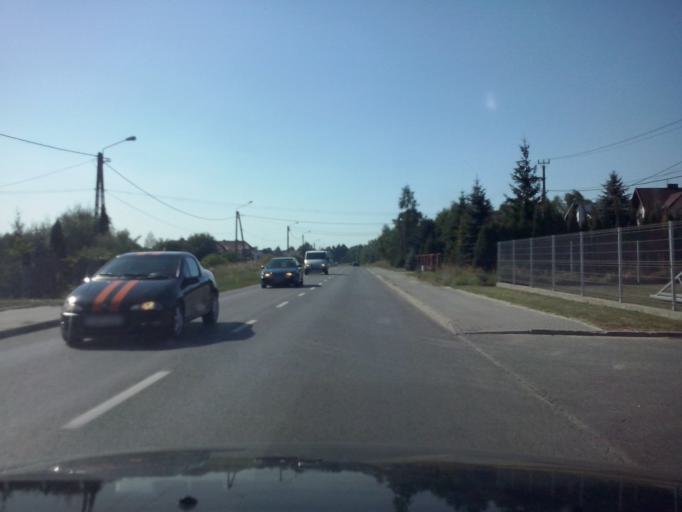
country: PL
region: Swietokrzyskie
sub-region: Powiat kielecki
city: Daleszyce
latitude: 50.8072
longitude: 20.7929
